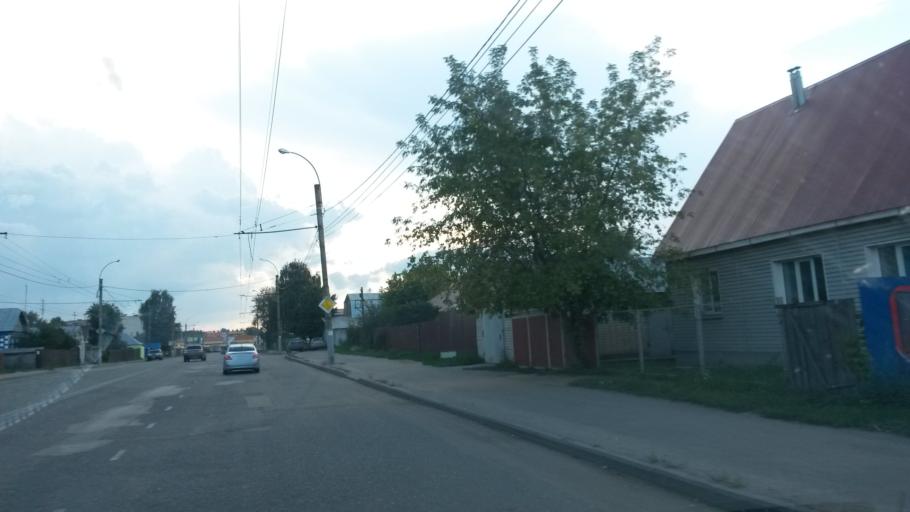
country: RU
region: Ivanovo
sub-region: Gorod Ivanovo
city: Ivanovo
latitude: 56.9591
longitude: 41.0063
